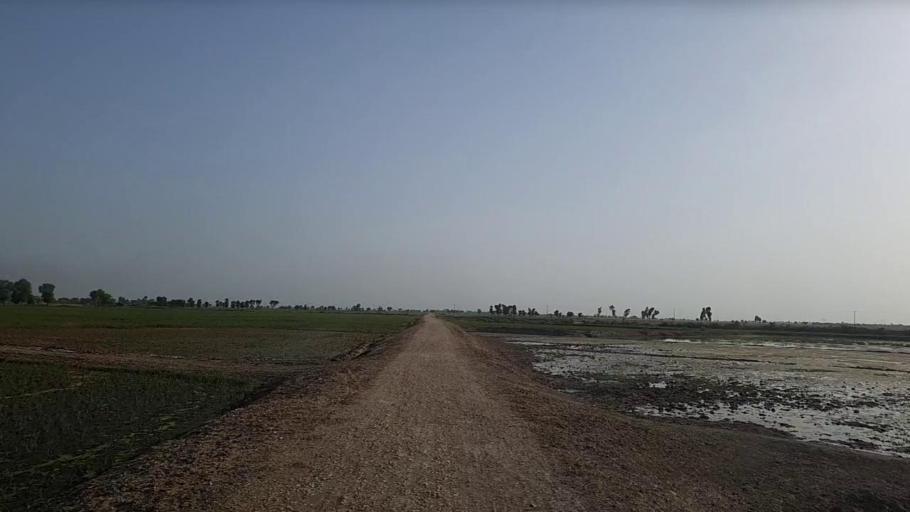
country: PK
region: Sindh
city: Sita Road
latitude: 27.1041
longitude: 67.8881
